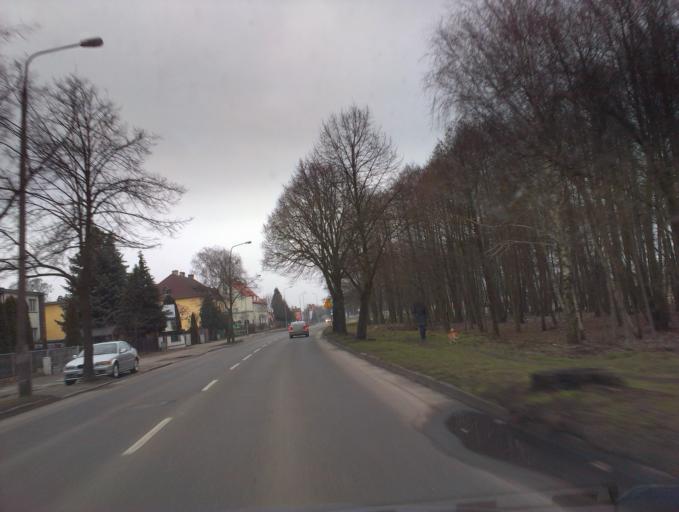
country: PL
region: Greater Poland Voivodeship
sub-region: Powiat pilski
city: Pila
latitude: 53.1609
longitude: 16.7374
